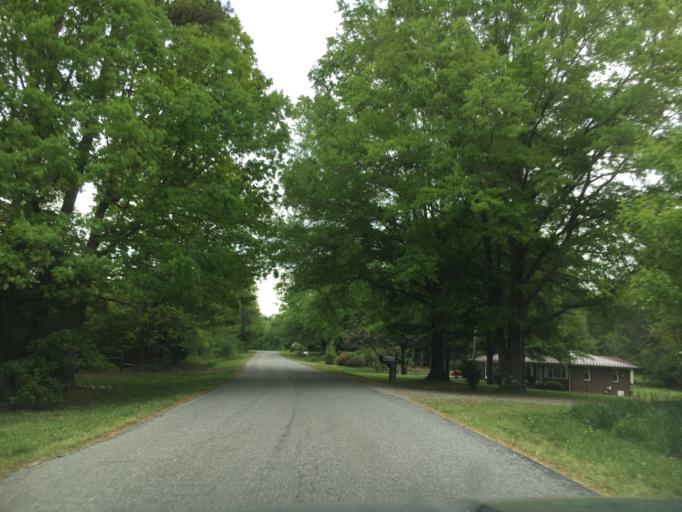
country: US
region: Virginia
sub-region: Halifax County
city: Halifax
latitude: 36.8018
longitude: -78.9197
